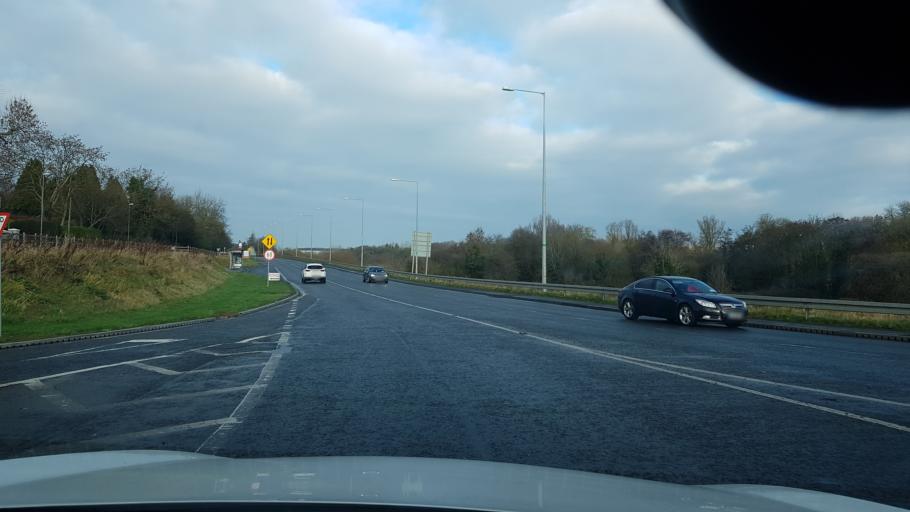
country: IE
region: Leinster
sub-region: An Mhi
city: Navan
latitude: 53.6341
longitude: -6.6651
